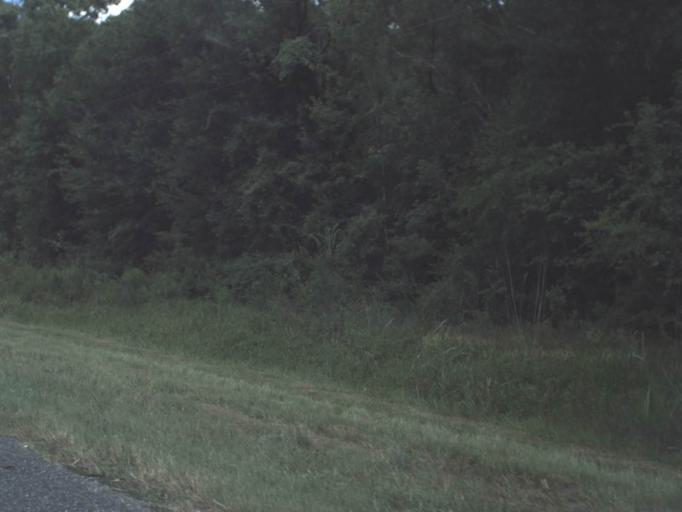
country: US
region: Florida
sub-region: Taylor County
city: Perry
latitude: 29.9620
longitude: -83.4702
